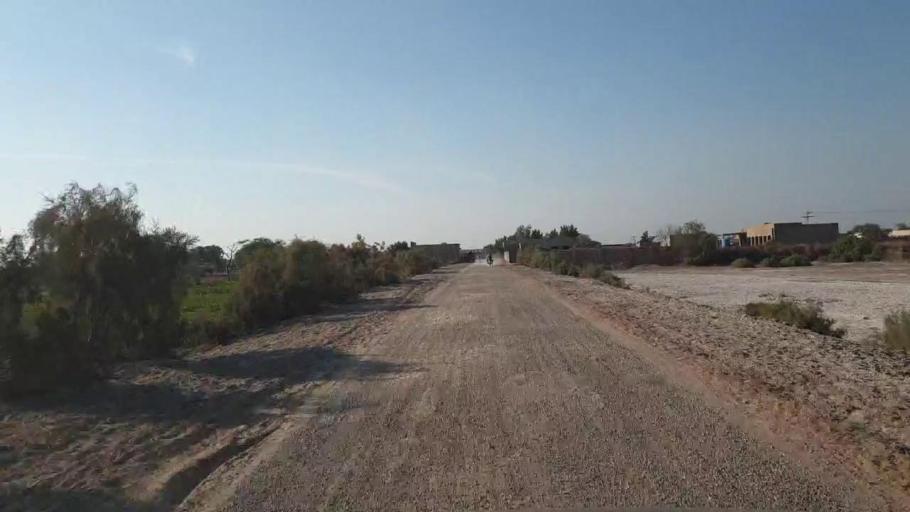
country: PK
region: Sindh
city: Shahpur Chakar
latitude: 26.1782
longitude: 68.6660
